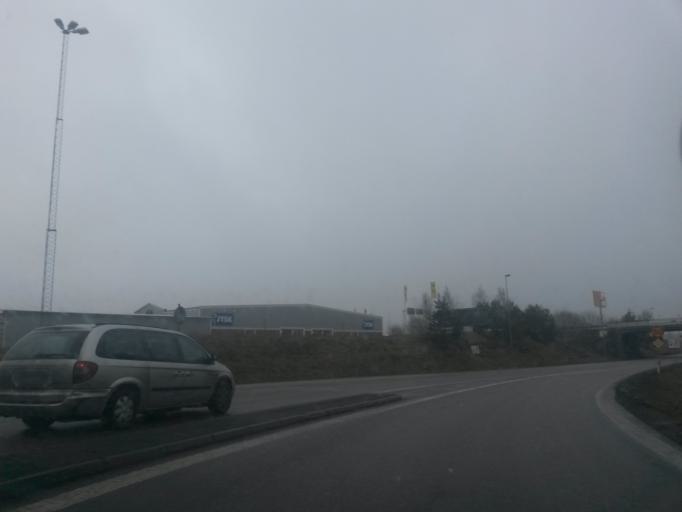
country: SE
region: Vaestra Goetaland
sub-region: Trollhattan
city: Trollhattan
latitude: 58.3173
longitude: 12.3086
